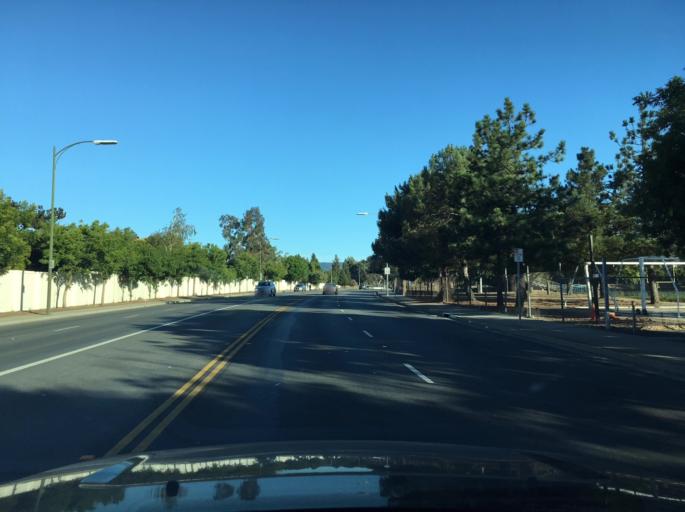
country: US
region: California
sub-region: Santa Clara County
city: Cambrian Park
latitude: 37.2536
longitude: -121.8969
